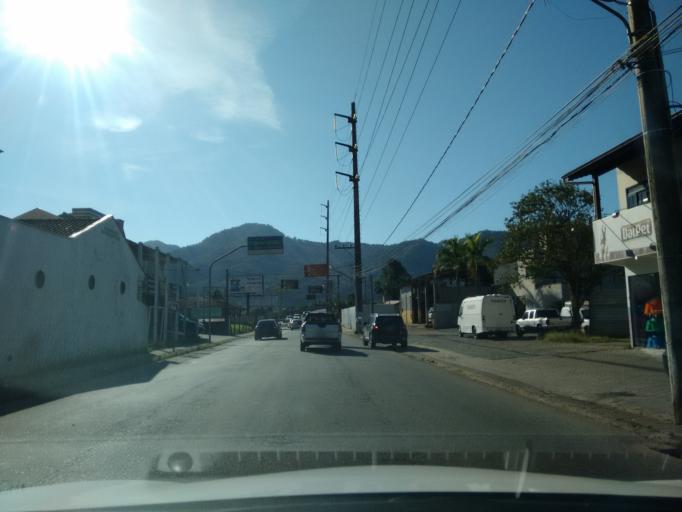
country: BR
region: Santa Catarina
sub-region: Jaragua Do Sul
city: Jaragua do Sul
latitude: -26.4895
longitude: -49.0560
